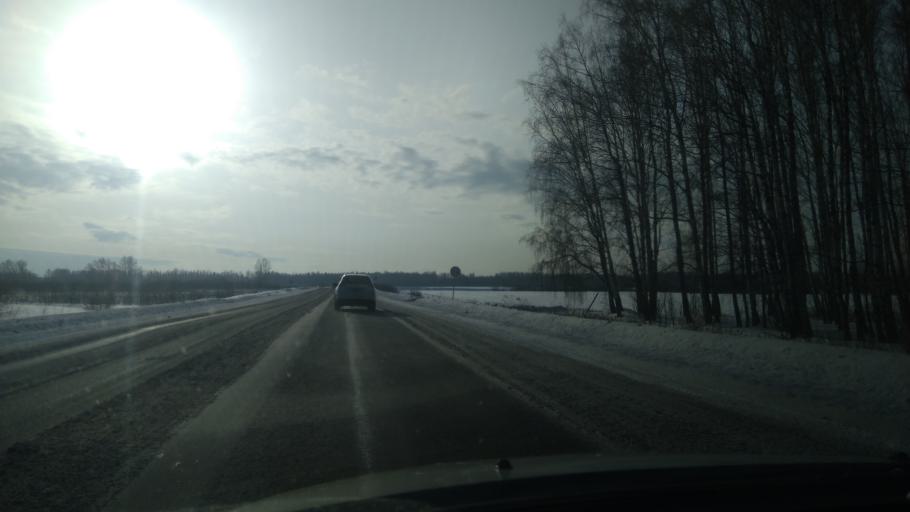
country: RU
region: Sverdlovsk
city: Bogdanovich
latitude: 56.7842
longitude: 61.9981
